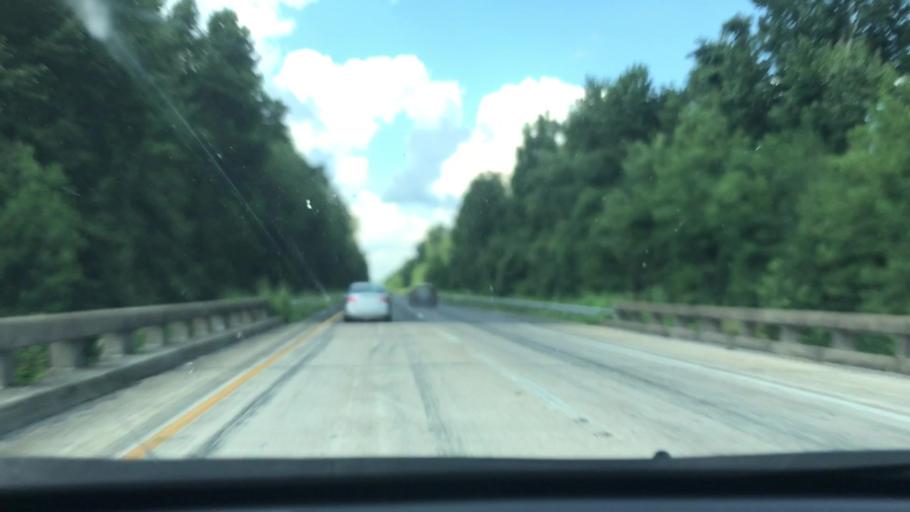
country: US
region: South Carolina
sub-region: Clarendon County
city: Manning
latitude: 33.8271
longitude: -80.1357
